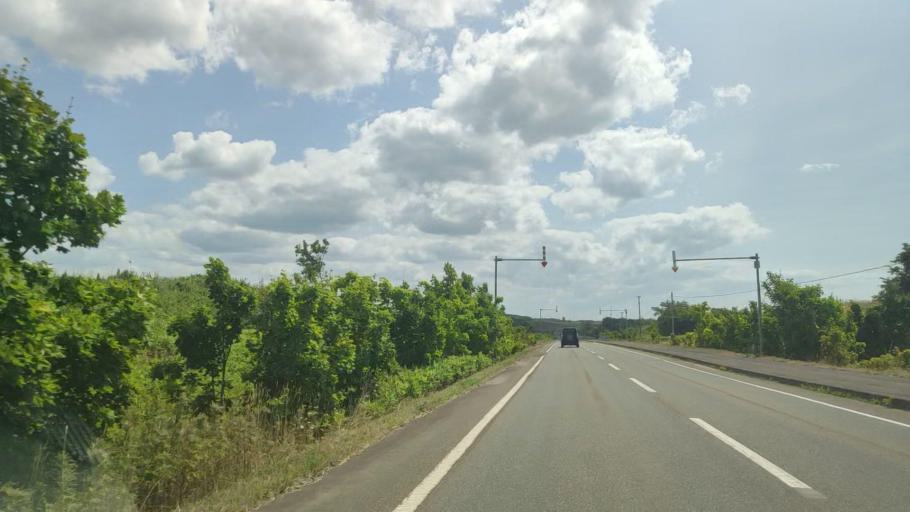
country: JP
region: Hokkaido
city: Makubetsu
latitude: 44.7983
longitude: 141.7881
